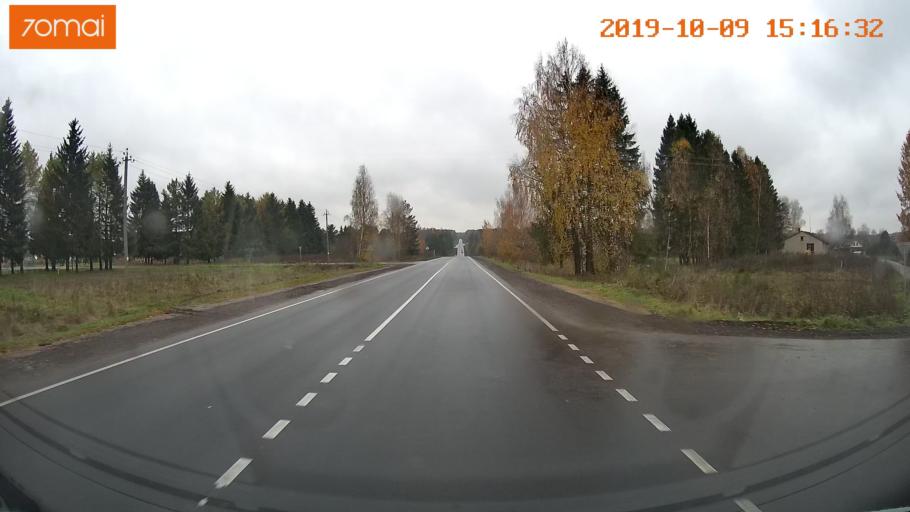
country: RU
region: Kostroma
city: Susanino
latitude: 58.1094
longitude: 41.5857
